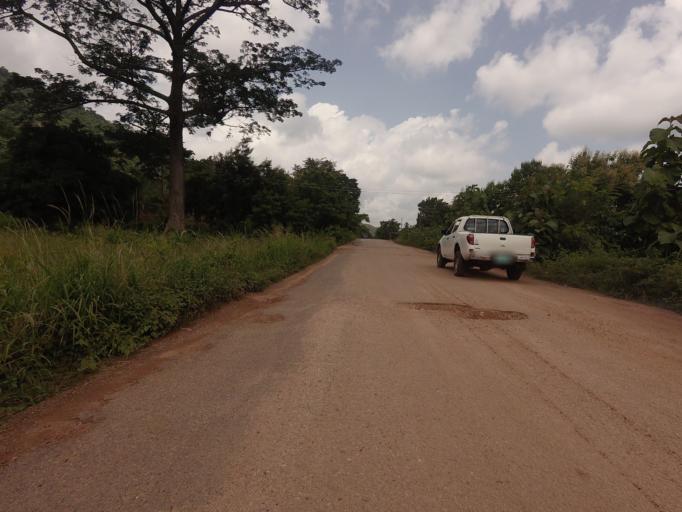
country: GH
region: Volta
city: Ho
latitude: 6.7309
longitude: 0.3464
